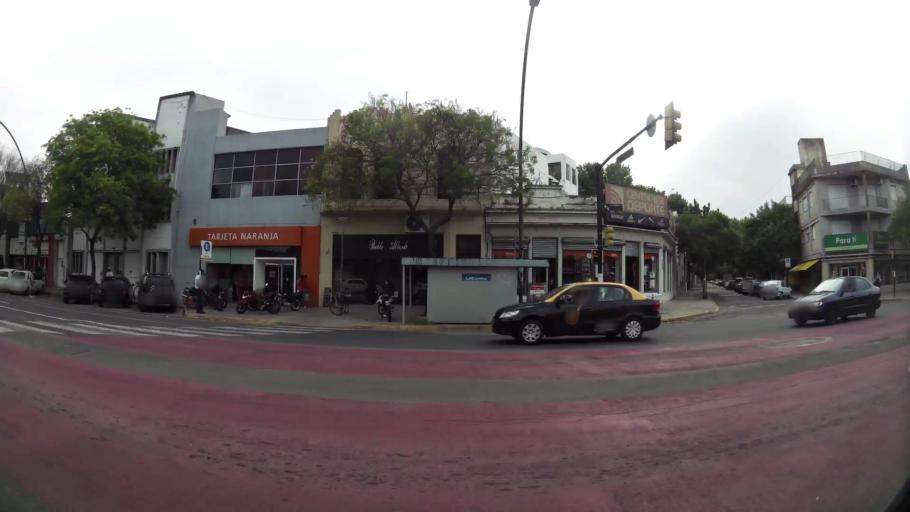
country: AR
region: Santa Fe
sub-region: Departamento de Rosario
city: Rosario
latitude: -32.9182
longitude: -60.6833
